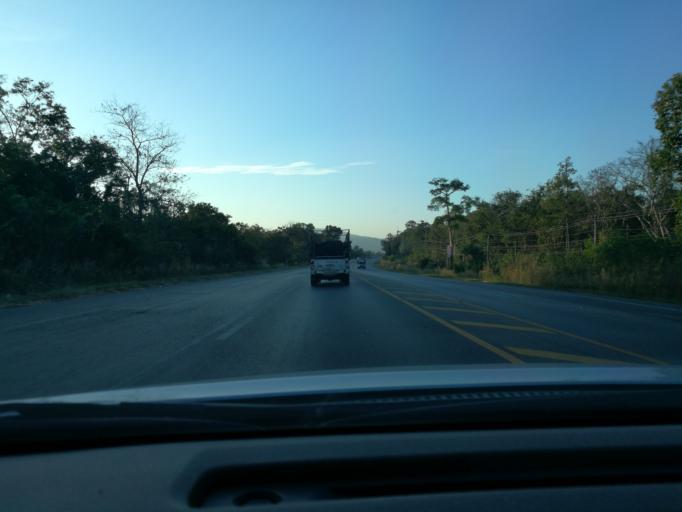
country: TH
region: Phitsanulok
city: Wang Thong
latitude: 16.8469
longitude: 100.5234
